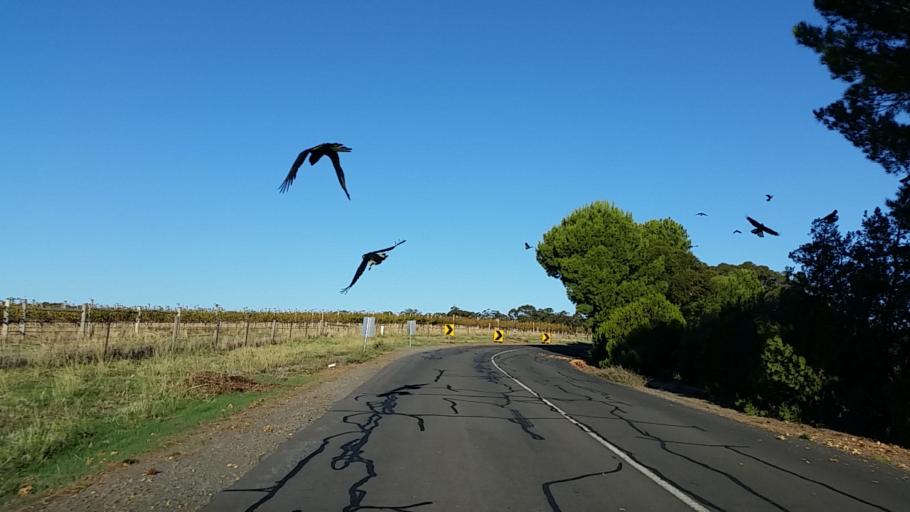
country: AU
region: South Australia
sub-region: Onkaparinga
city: Hackham
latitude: -35.1529
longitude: 138.5414
